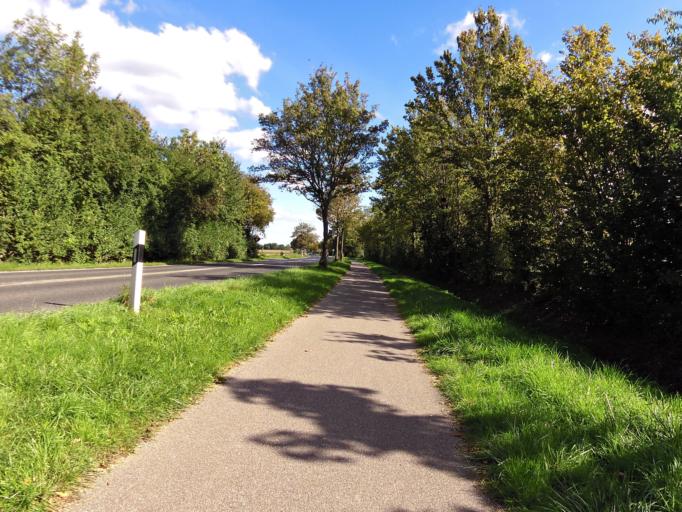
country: DE
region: North Rhine-Westphalia
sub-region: Regierungsbezirk Koln
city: Euskirchen
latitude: 50.6247
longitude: 6.8270
